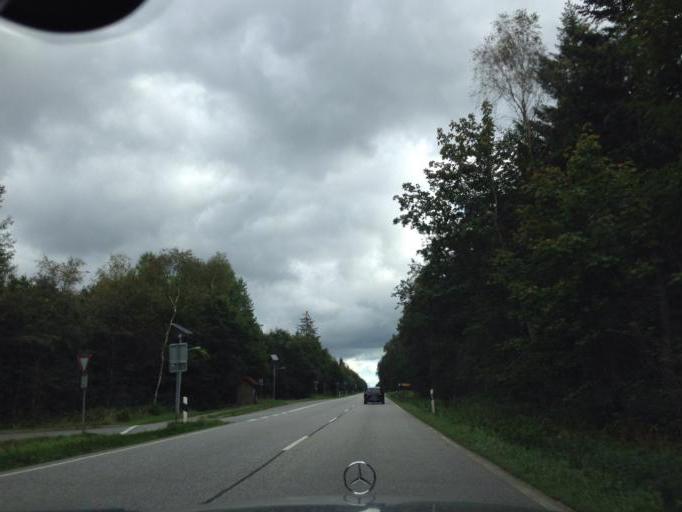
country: DE
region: Schleswig-Holstein
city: Stadum
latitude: 54.7492
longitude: 9.0174
